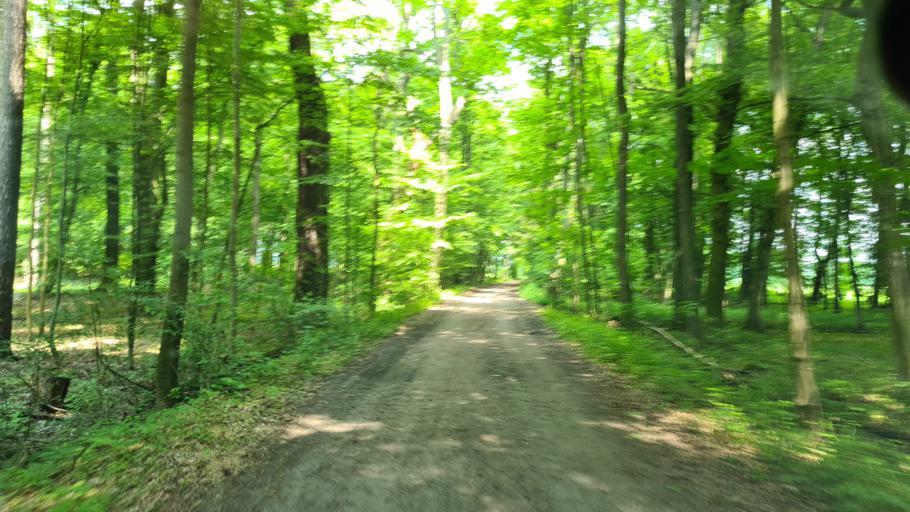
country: DE
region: Brandenburg
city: Sonnewalde
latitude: 51.7023
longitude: 13.6376
